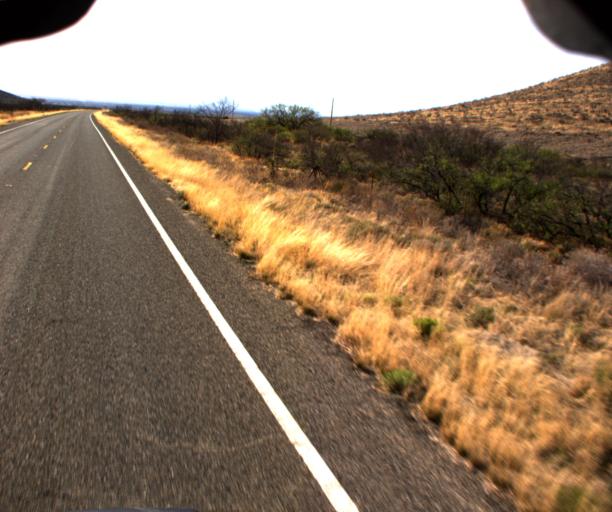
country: US
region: Arizona
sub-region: Cochise County
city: Willcox
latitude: 32.1838
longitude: -109.6686
